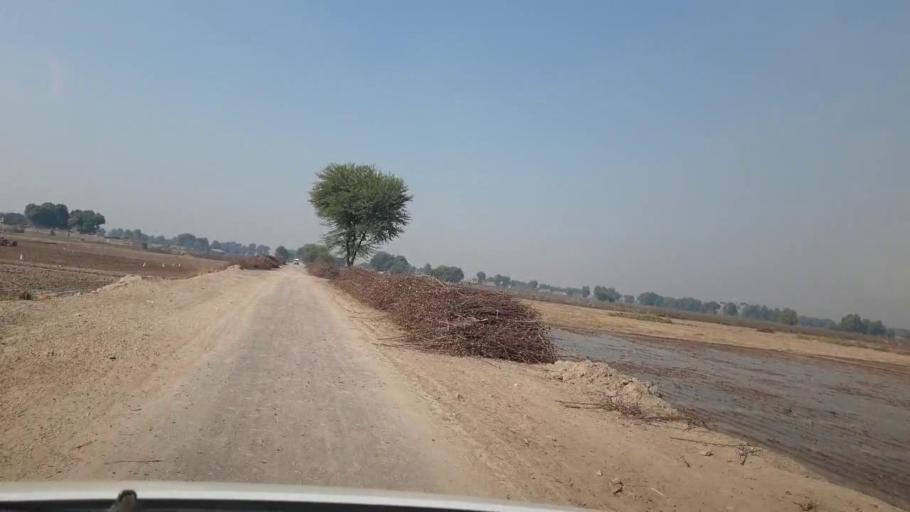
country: PK
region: Sindh
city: Bhan
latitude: 26.6117
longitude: 67.7715
